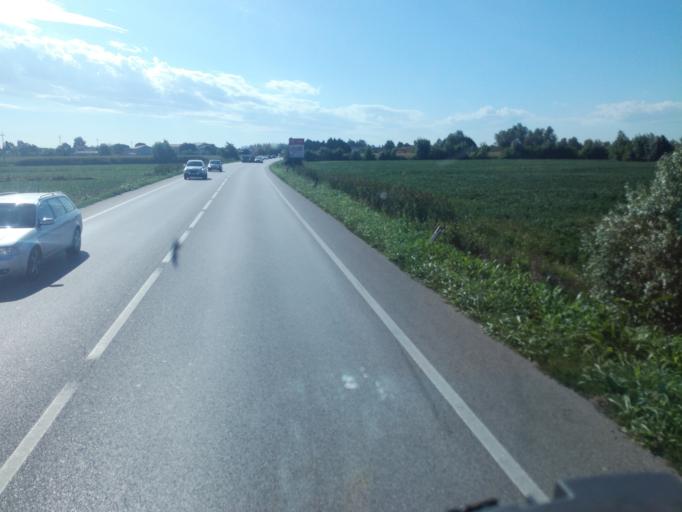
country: IT
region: Veneto
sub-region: Provincia di Padova
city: Vallonga
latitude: 45.2798
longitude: 12.0844
